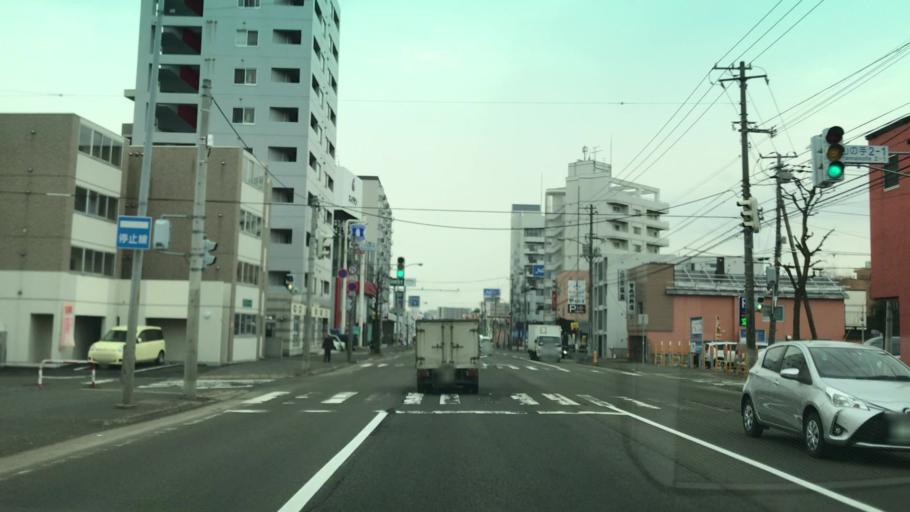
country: JP
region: Hokkaido
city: Sapporo
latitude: 43.0709
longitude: 141.3032
